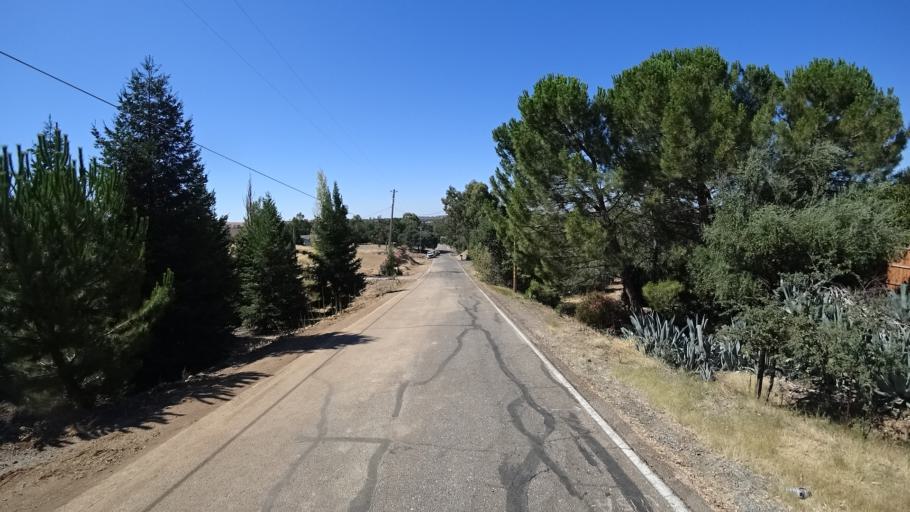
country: US
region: California
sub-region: Calaveras County
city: Rancho Calaveras
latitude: 38.1051
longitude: -120.8713
